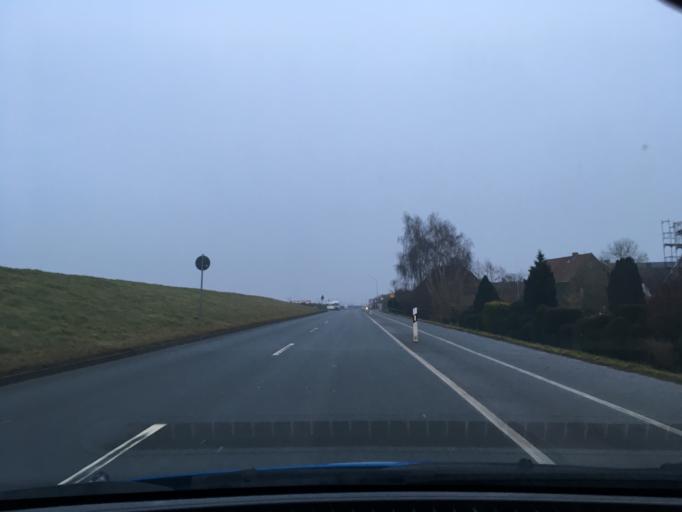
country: DE
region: Lower Saxony
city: Stelle
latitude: 53.4170
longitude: 10.1383
